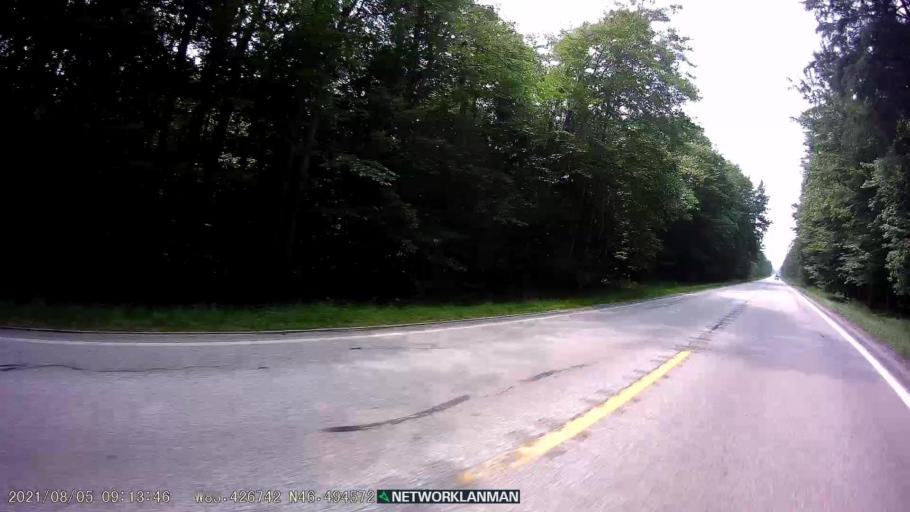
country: US
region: Michigan
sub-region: Luce County
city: Newberry
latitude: 46.4943
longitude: -85.4268
